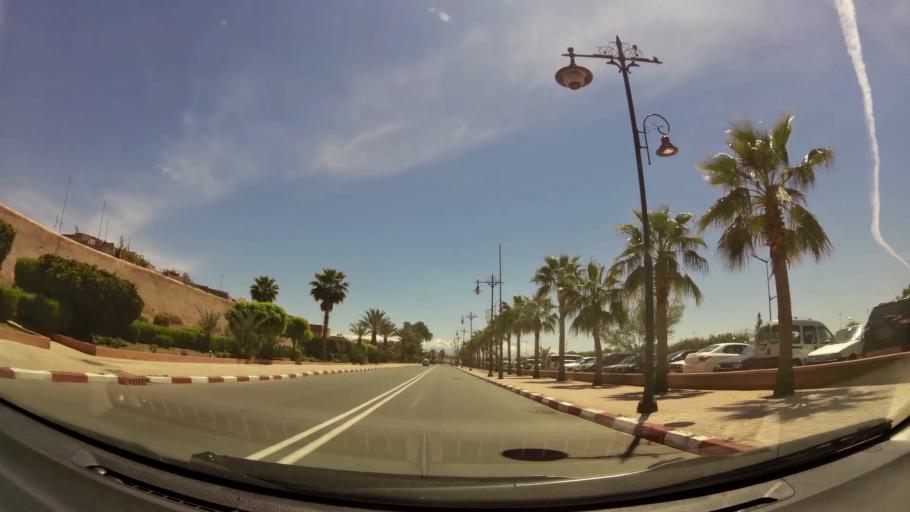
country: MA
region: Marrakech-Tensift-Al Haouz
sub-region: Marrakech
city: Marrakesh
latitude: 31.6143
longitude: -7.9900
